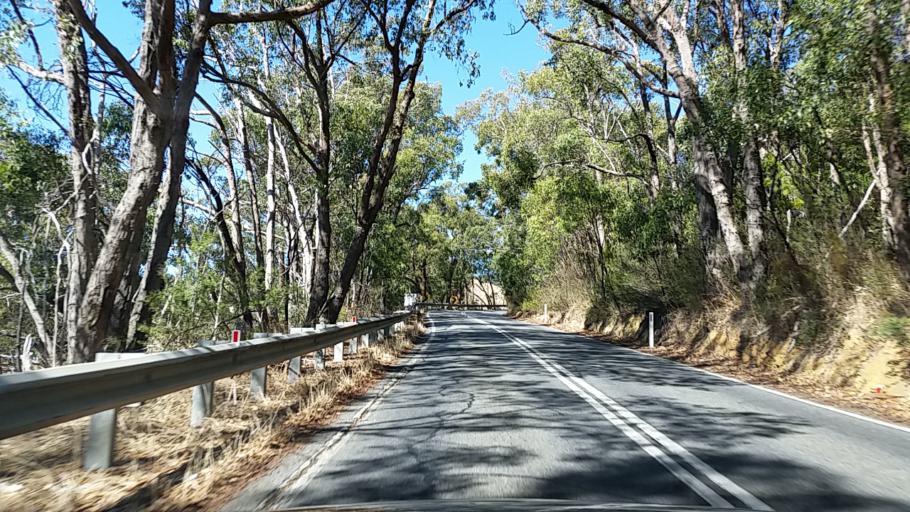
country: AU
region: South Australia
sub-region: Burnside
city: Wattle Park
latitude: -34.9555
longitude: 138.7027
